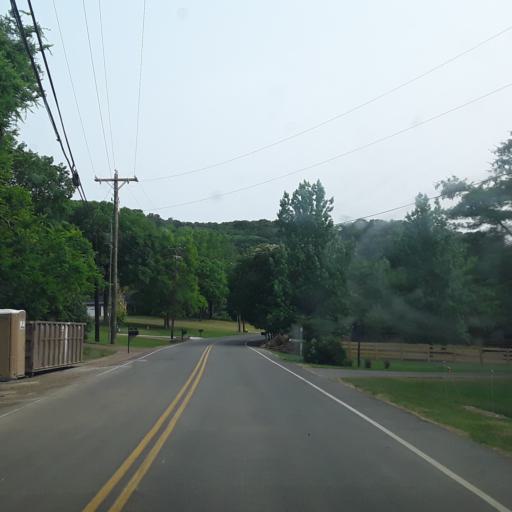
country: US
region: Tennessee
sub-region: Williamson County
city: Brentwood
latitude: 36.0508
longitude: -86.7812
